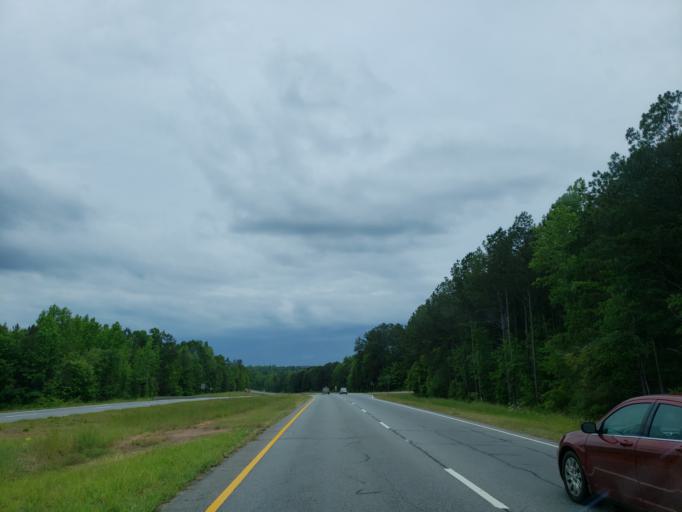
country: US
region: Georgia
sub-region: Haralson County
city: Bremen
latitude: 33.7390
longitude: -85.1658
